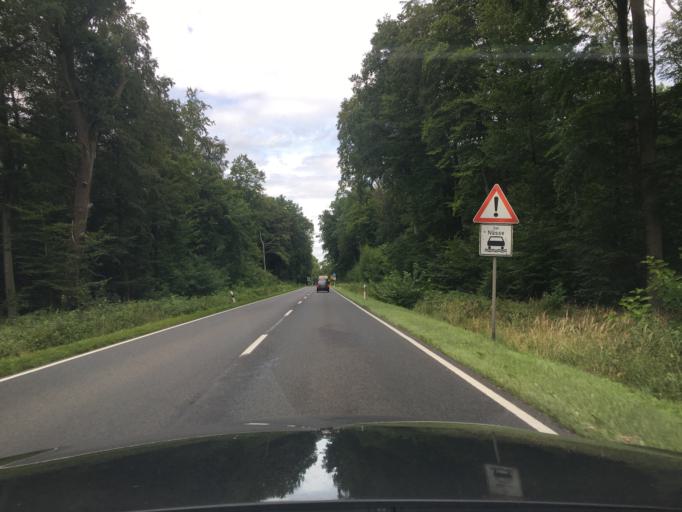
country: DE
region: Brandenburg
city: Gransee
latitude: 53.0676
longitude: 13.1837
